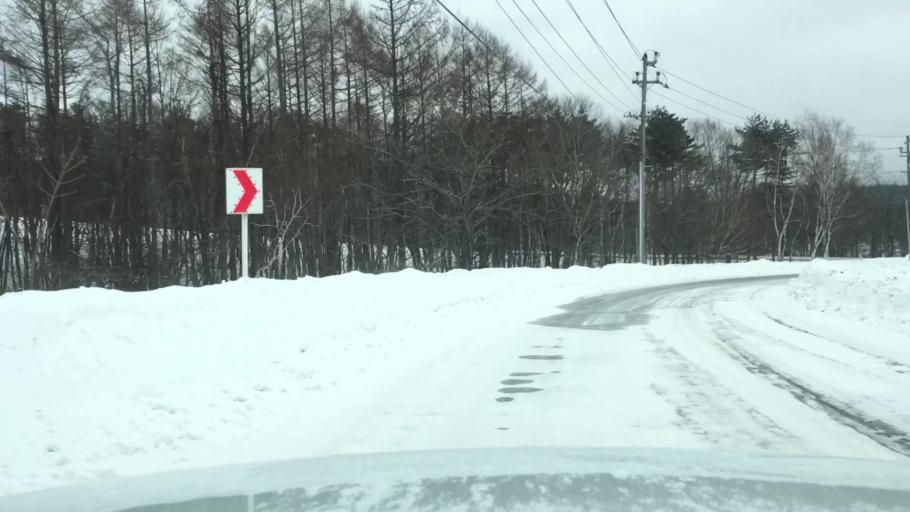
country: JP
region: Iwate
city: Shizukuishi
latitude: 39.9708
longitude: 140.9959
